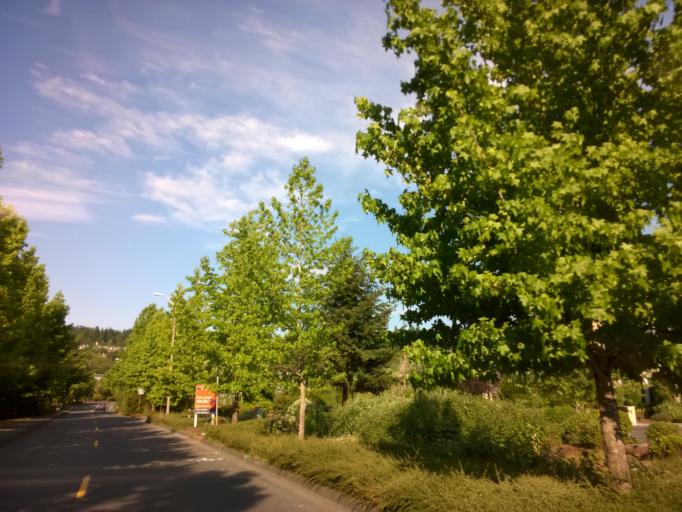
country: US
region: Washington
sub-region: King County
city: Bothell
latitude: 47.7782
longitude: -122.1882
